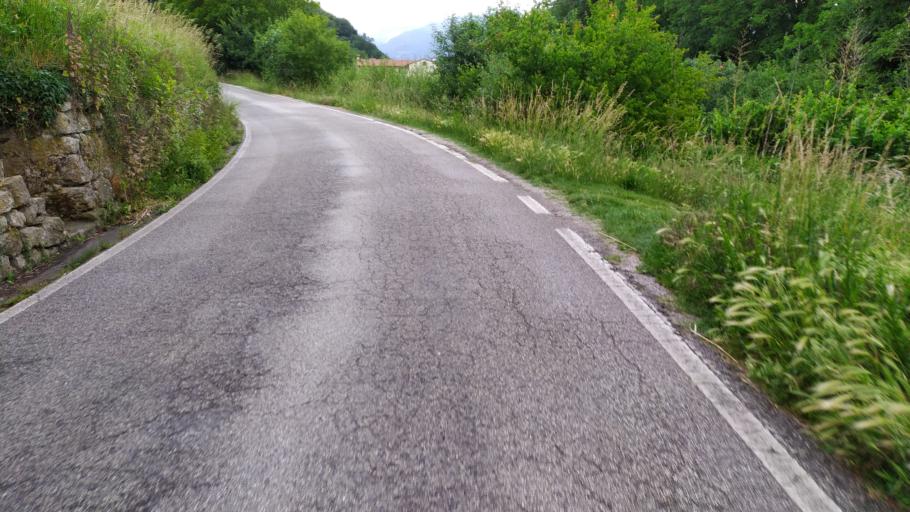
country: IT
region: Veneto
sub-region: Provincia di Vicenza
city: Malo
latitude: 45.6454
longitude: 11.4198
